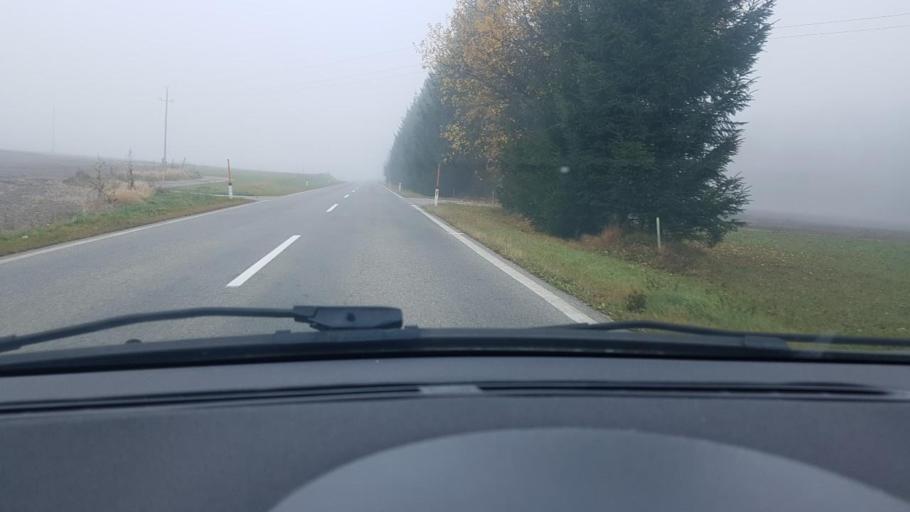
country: AT
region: Carinthia
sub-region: Politischer Bezirk Volkermarkt
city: Eberndorf
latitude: 46.5591
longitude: 14.6410
